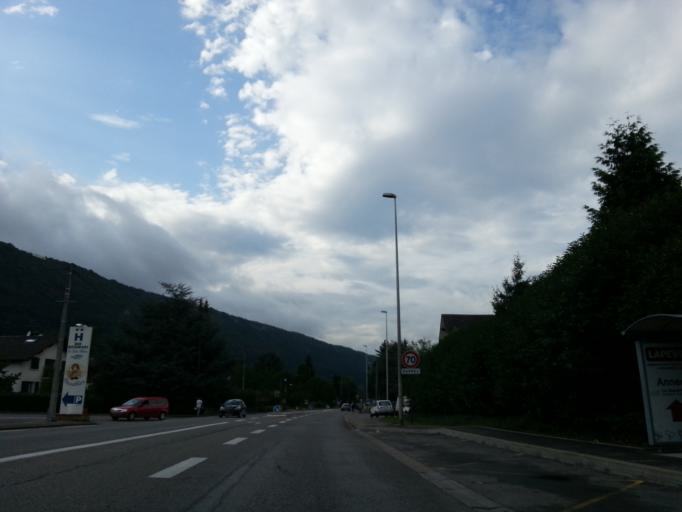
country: FR
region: Rhone-Alpes
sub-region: Departement de la Haute-Savoie
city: Sevrier
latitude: 45.8475
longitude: 6.1466
